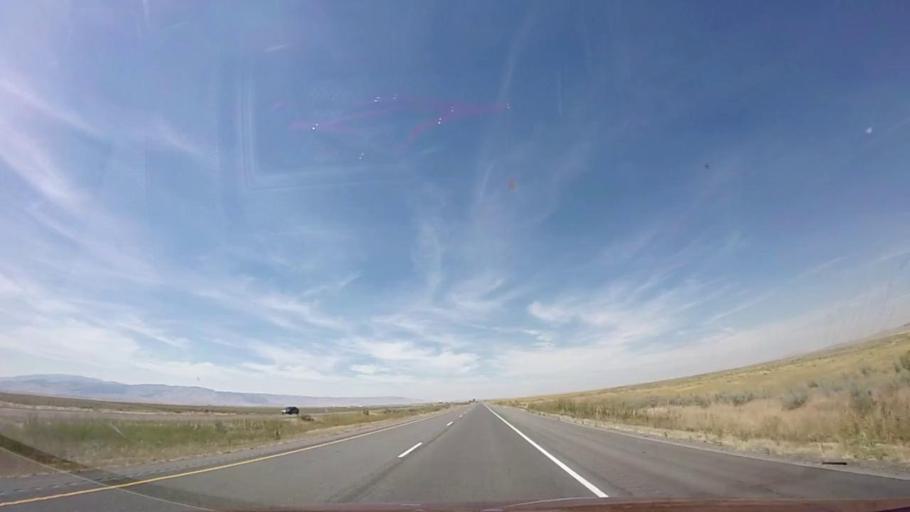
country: US
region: Idaho
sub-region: Minidoka County
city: Rupert
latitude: 42.3073
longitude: -113.1860
